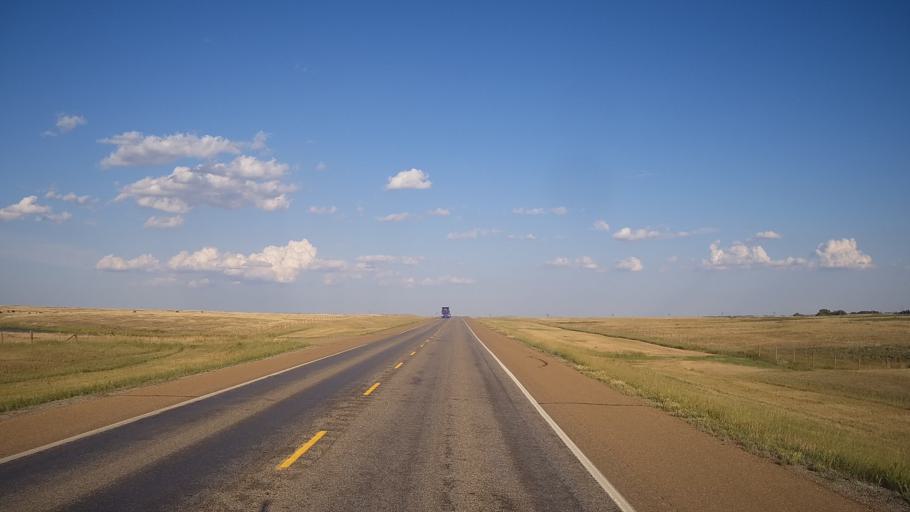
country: CA
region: Alberta
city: Hanna
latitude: 51.6253
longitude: -111.8868
